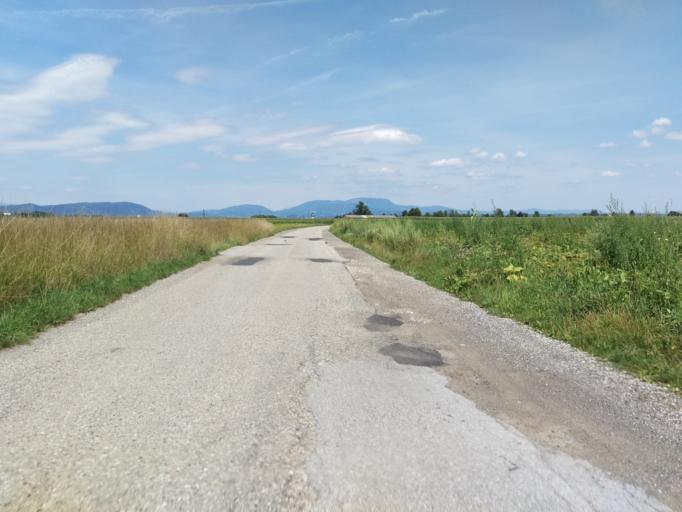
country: AT
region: Styria
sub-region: Politischer Bezirk Graz-Umgebung
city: Kalsdorf bei Graz
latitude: 46.9702
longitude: 15.4473
